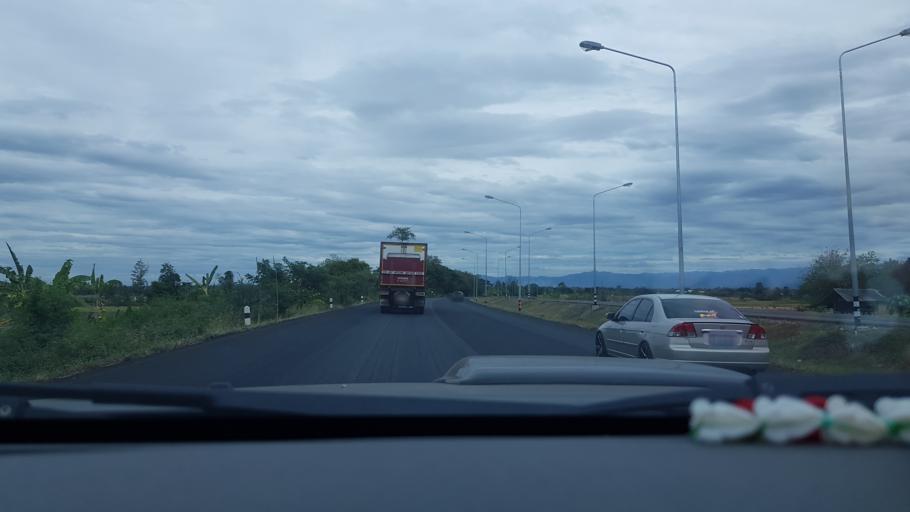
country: TH
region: Phetchabun
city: Phetchabun
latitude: 16.4922
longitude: 101.1428
